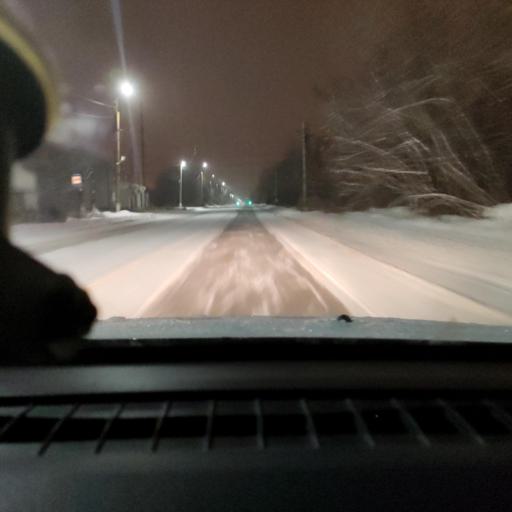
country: RU
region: Samara
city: Novokuybyshevsk
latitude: 53.0828
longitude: 49.9394
